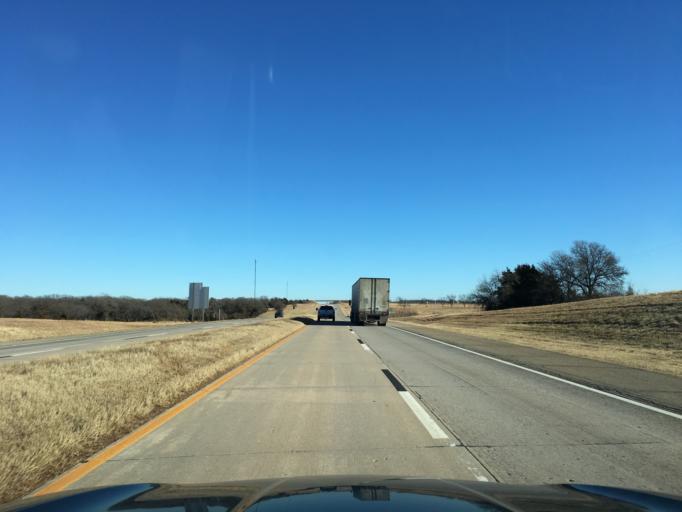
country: US
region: Oklahoma
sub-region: Pawnee County
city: Pawnee
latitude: 36.2246
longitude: -96.7612
